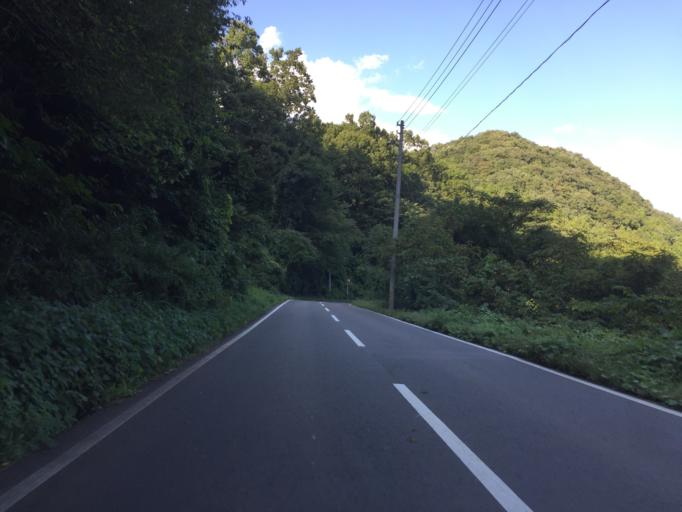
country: JP
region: Fukushima
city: Hobaramachi
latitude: 37.7430
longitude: 140.5492
